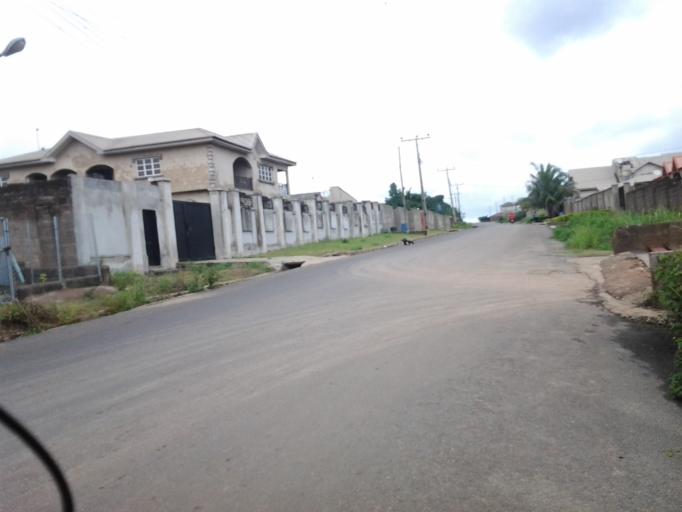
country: NG
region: Oyo
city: Ibadan
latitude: 7.4363
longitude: 3.9589
